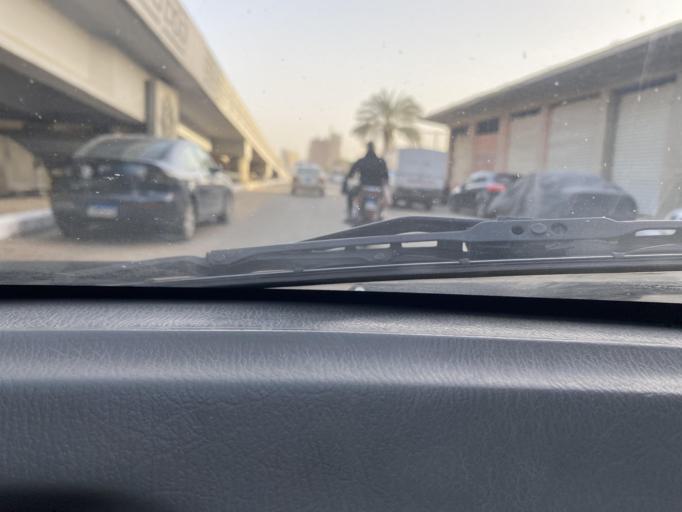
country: EG
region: Muhafazat al Qahirah
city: Cairo
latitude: 30.1184
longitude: 31.2968
